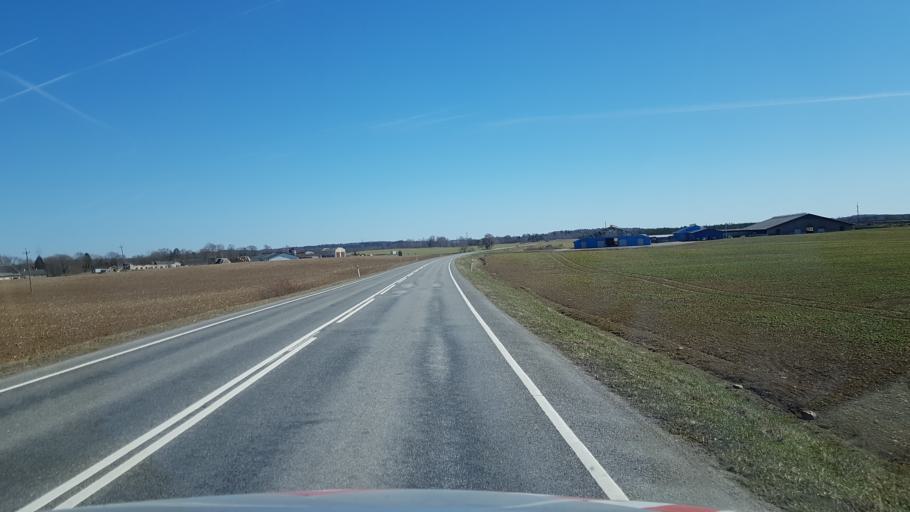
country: EE
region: Laeaene-Virumaa
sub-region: Vinni vald
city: Vinni
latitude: 59.3253
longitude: 26.4251
